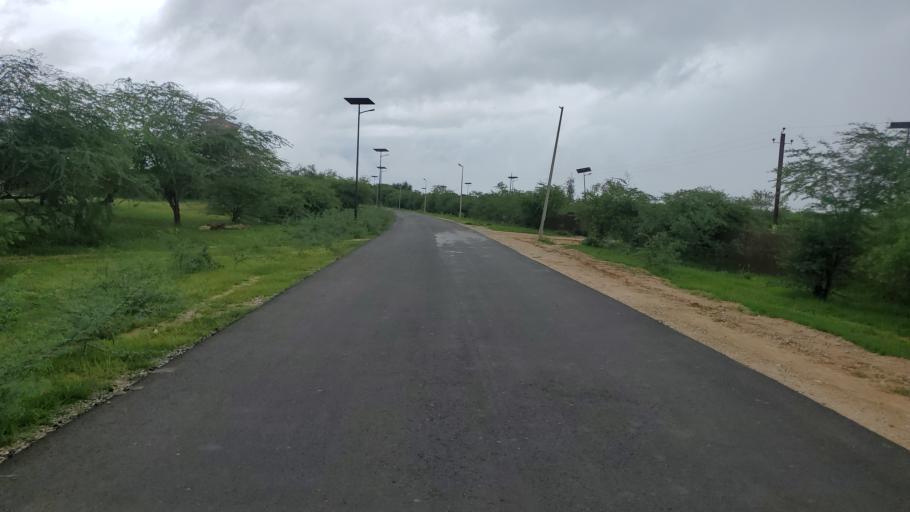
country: SN
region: Saint-Louis
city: Saint-Louis
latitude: 16.0603
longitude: -16.4283
